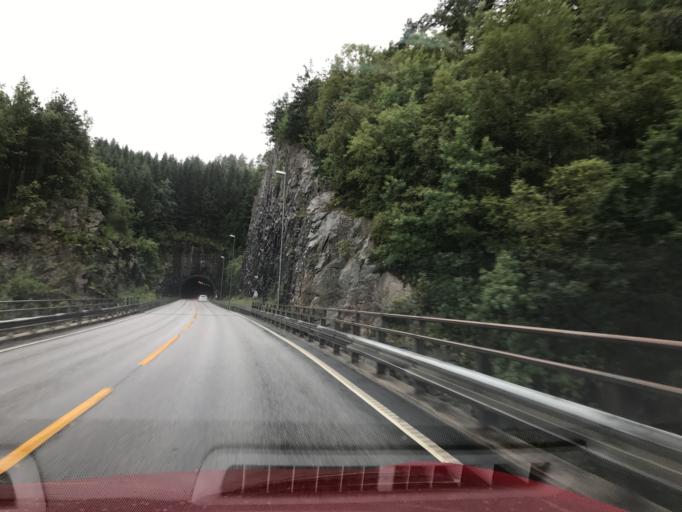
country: NO
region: Vest-Agder
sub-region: Flekkefjord
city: Flekkefjord
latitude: 58.2733
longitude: 6.7783
